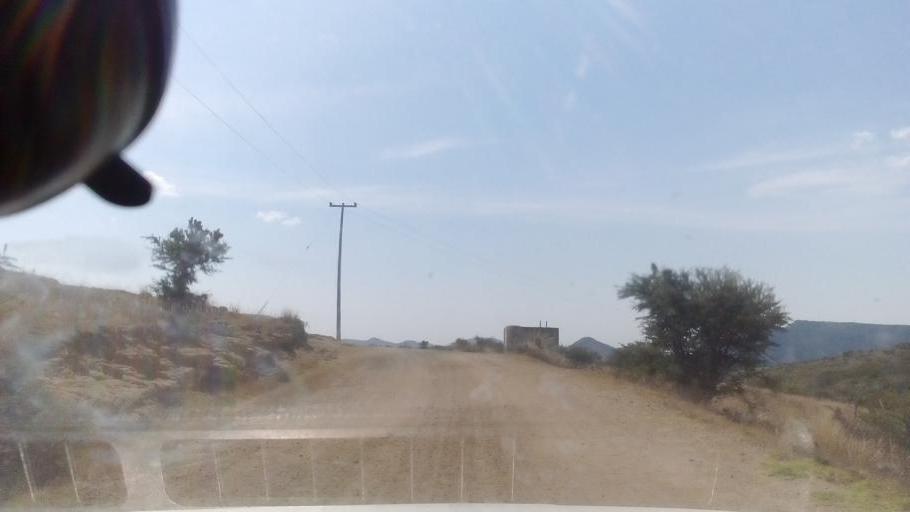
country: MX
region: Guanajuato
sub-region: Leon
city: Lucio Blanco (Los Gavilanes)
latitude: 21.1937
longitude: -101.4972
